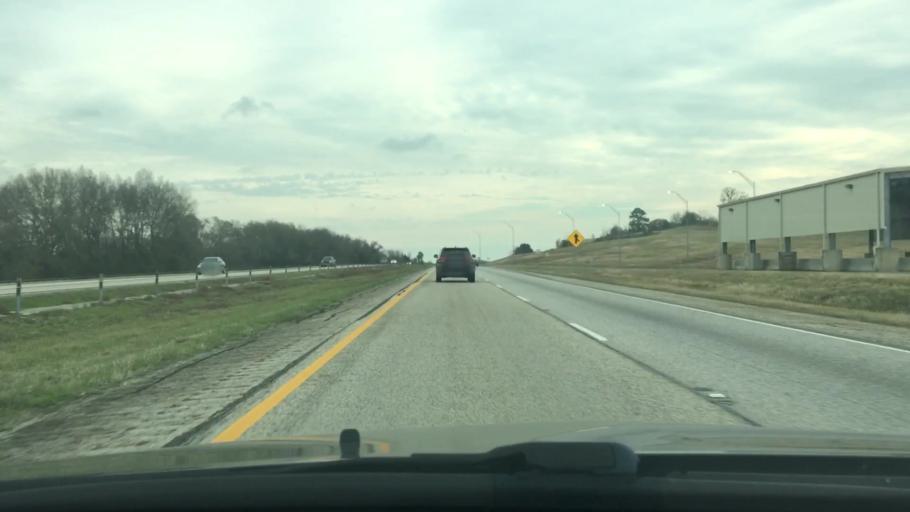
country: US
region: Texas
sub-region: Leon County
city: Centerville
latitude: 31.2791
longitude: -95.9904
